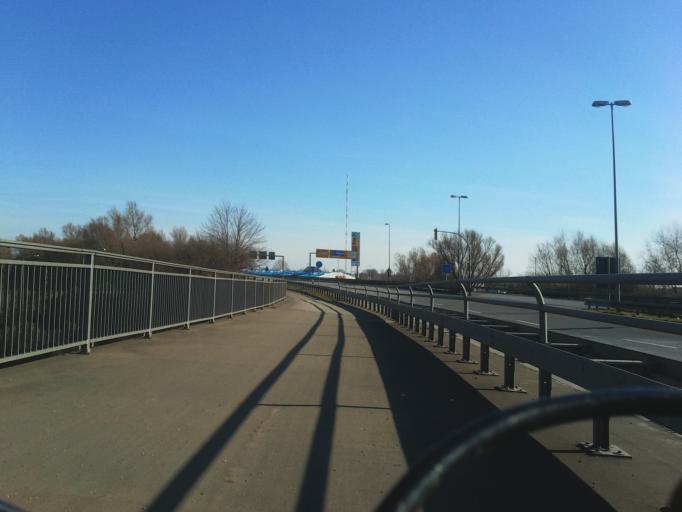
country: DE
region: Mecklenburg-Vorpommern
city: Warnemuende
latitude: 54.1407
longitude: 12.1113
